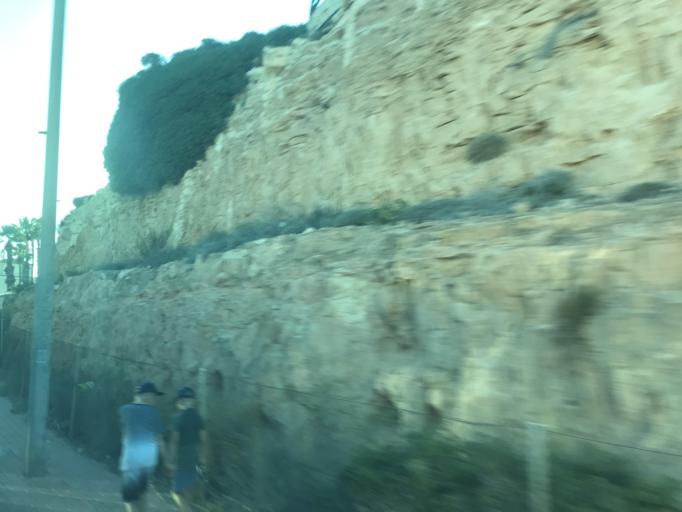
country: ES
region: Valencia
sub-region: Provincia de Alicante
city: Torrevieja
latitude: 37.9999
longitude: -0.6512
